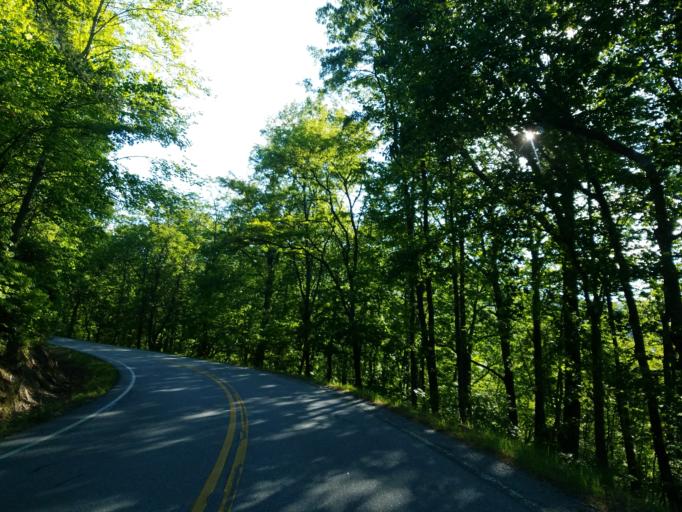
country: US
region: Georgia
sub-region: Fannin County
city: Blue Ridge
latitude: 34.8112
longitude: -84.1868
